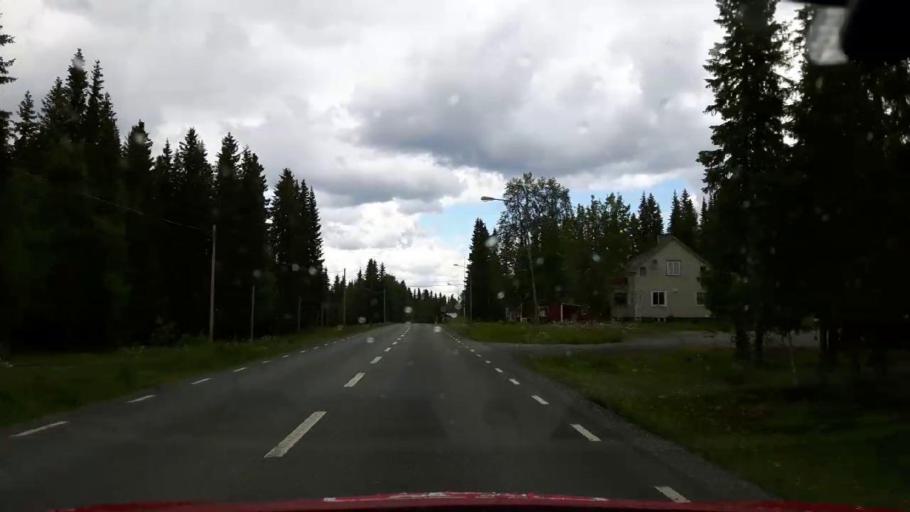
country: SE
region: Jaemtland
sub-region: Krokoms Kommun
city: Krokom
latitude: 63.7546
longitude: 14.3012
